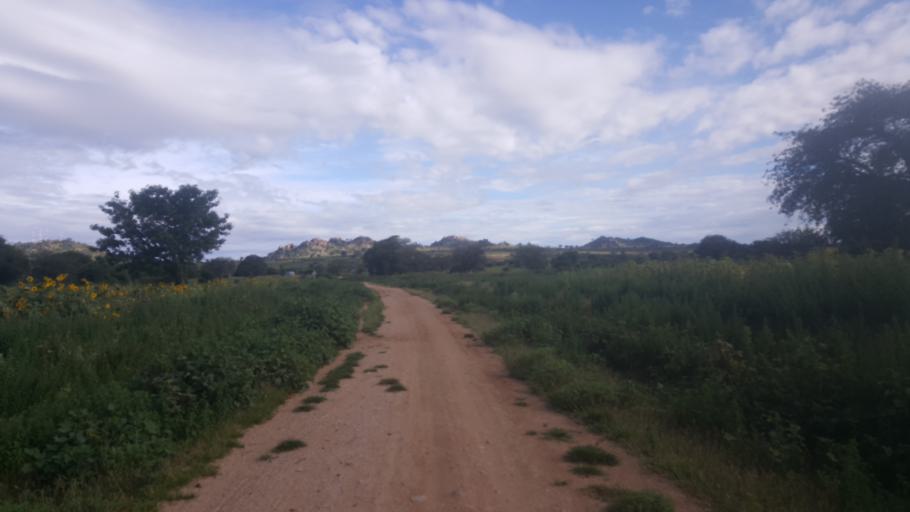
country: TZ
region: Dodoma
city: Dodoma
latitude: -6.0830
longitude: 35.5200
